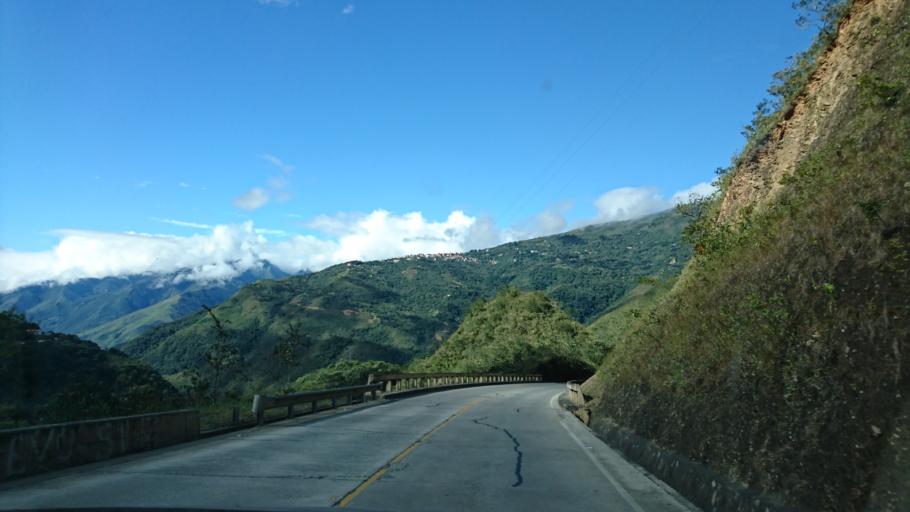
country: BO
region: La Paz
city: Coroico
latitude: -16.2013
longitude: -67.7596
